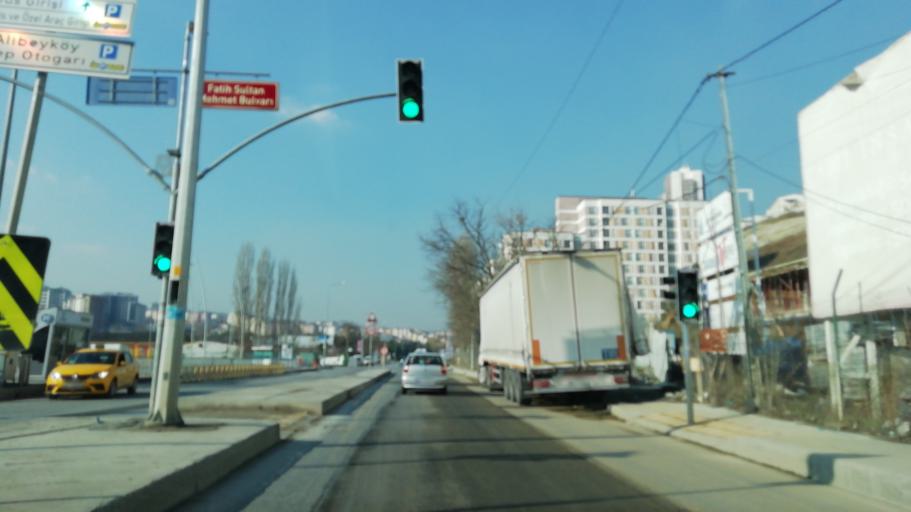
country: TR
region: Istanbul
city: Sisli
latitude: 41.0883
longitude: 28.9444
